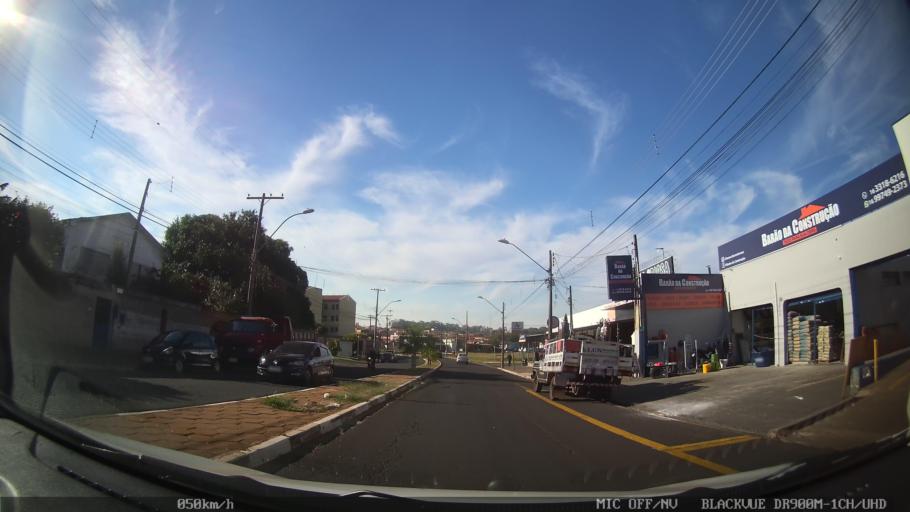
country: BR
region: Sao Paulo
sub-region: Araraquara
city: Araraquara
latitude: -21.7728
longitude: -48.1413
